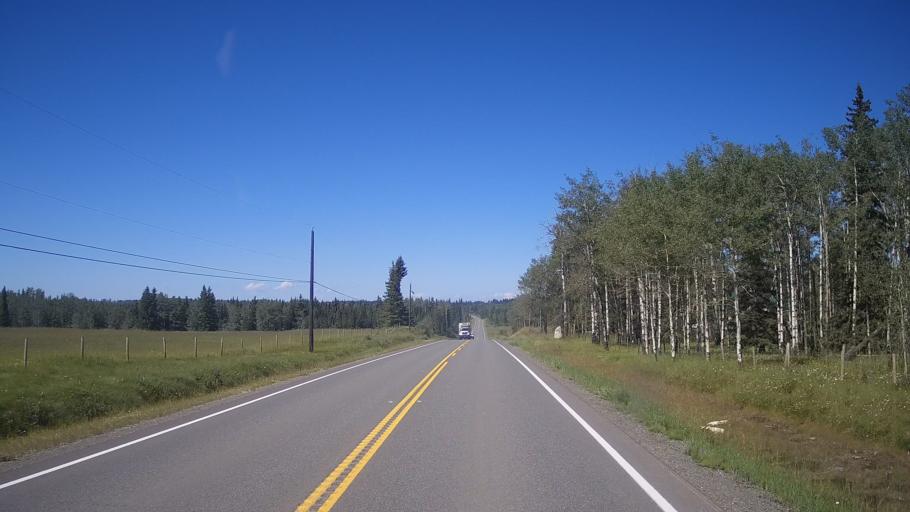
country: CA
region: British Columbia
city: Cache Creek
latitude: 51.5447
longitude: -120.9470
